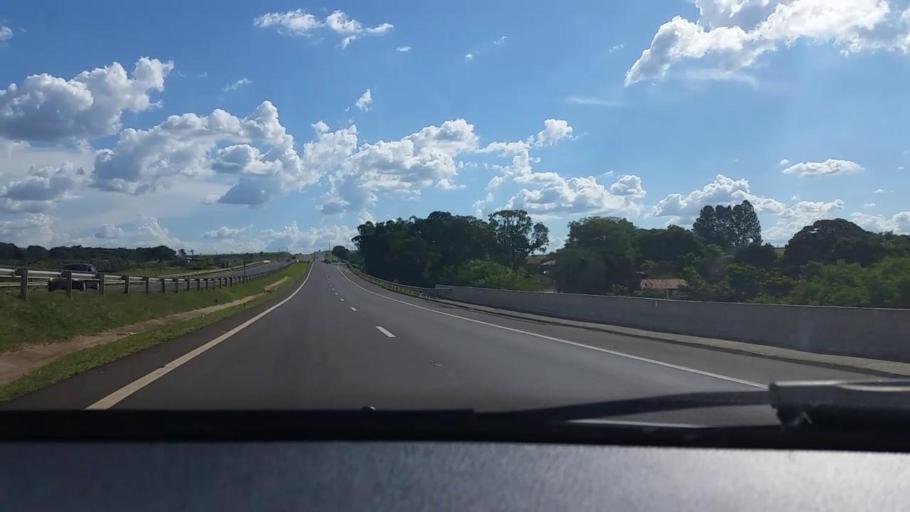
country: BR
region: Sao Paulo
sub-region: Bauru
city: Bauru
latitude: -22.3839
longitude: -49.0692
